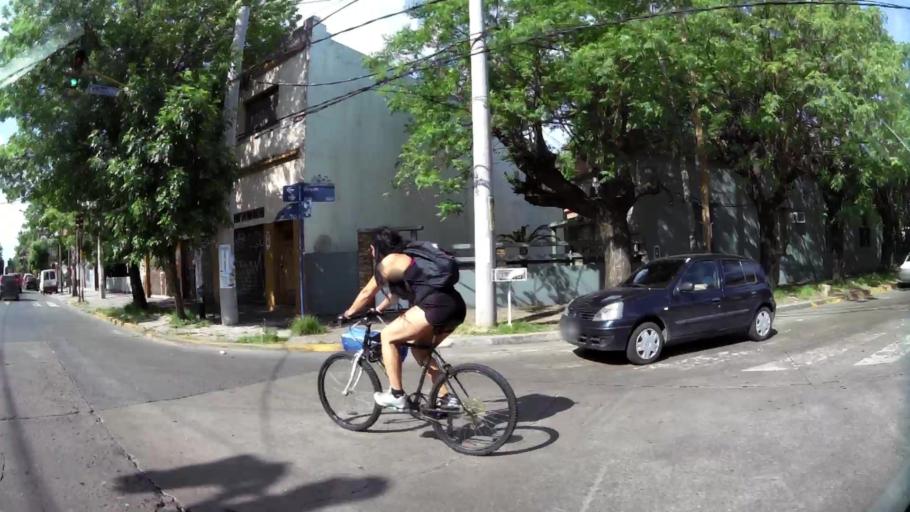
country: AR
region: Buenos Aires
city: San Justo
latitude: -34.6677
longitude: -58.5607
